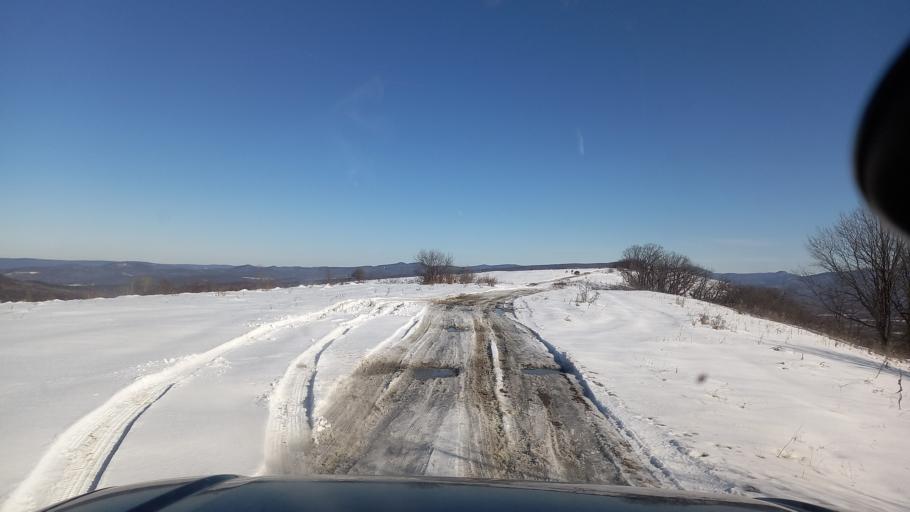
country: RU
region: Adygeya
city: Kamennomostskiy
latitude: 44.2279
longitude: 40.1173
